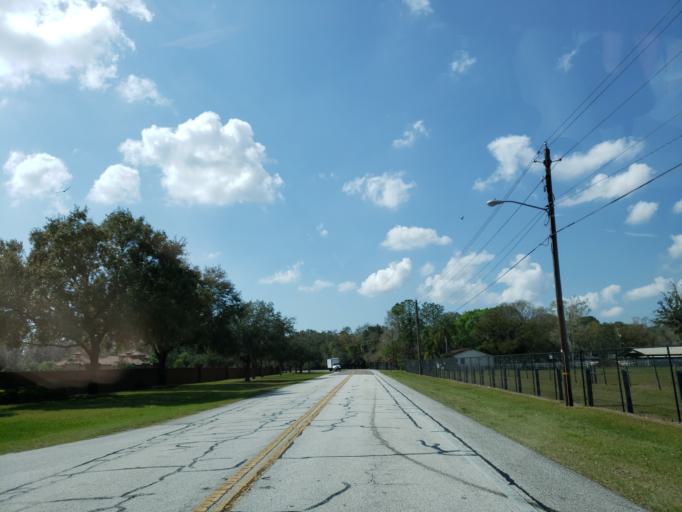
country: US
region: Florida
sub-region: Hillsborough County
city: Keystone
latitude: 28.1496
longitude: -82.5886
